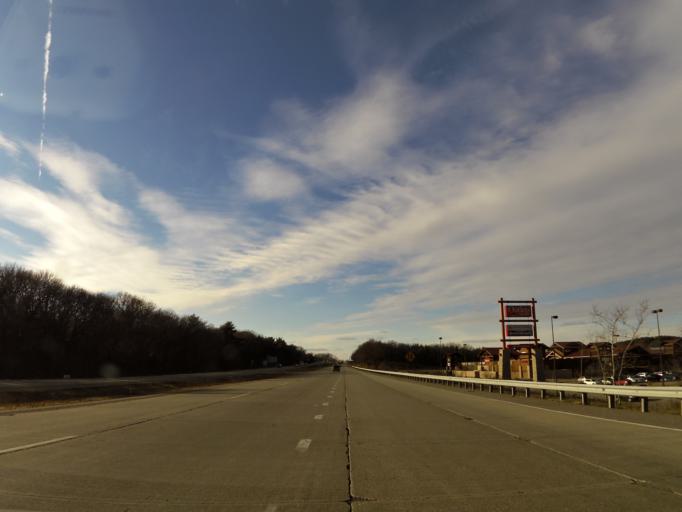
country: US
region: Wisconsin
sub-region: Sauk County
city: Lake Delton
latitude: 43.5704
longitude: -89.7835
